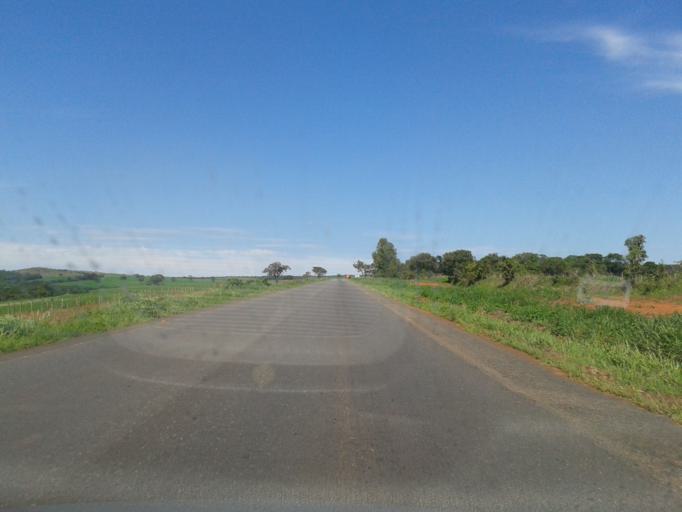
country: BR
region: Goias
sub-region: Bela Vista De Goias
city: Bela Vista de Goias
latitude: -17.1646
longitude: -48.7737
